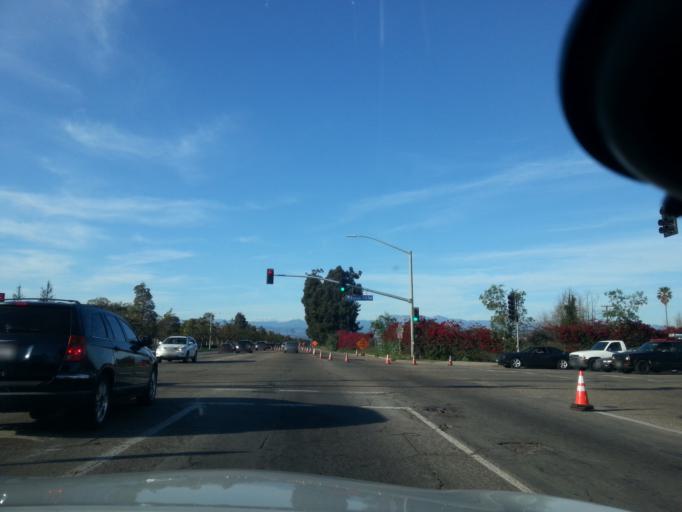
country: US
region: California
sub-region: Ventura County
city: Oxnard
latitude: 34.2060
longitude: -119.1596
